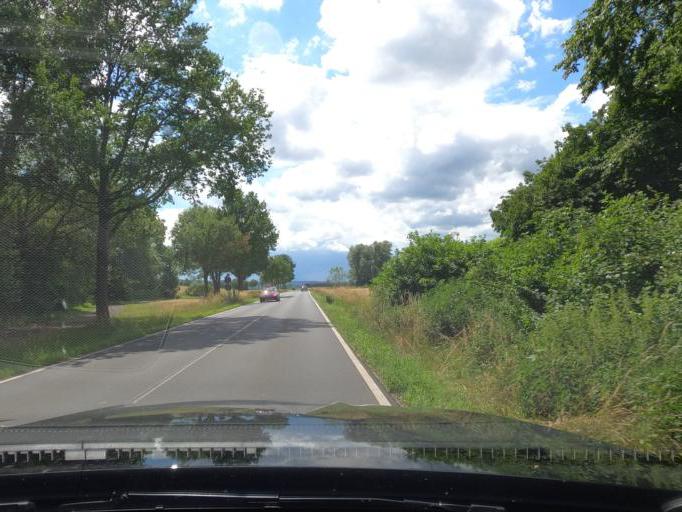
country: DE
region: Lower Saxony
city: Lengede
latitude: 52.1608
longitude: 10.2977
